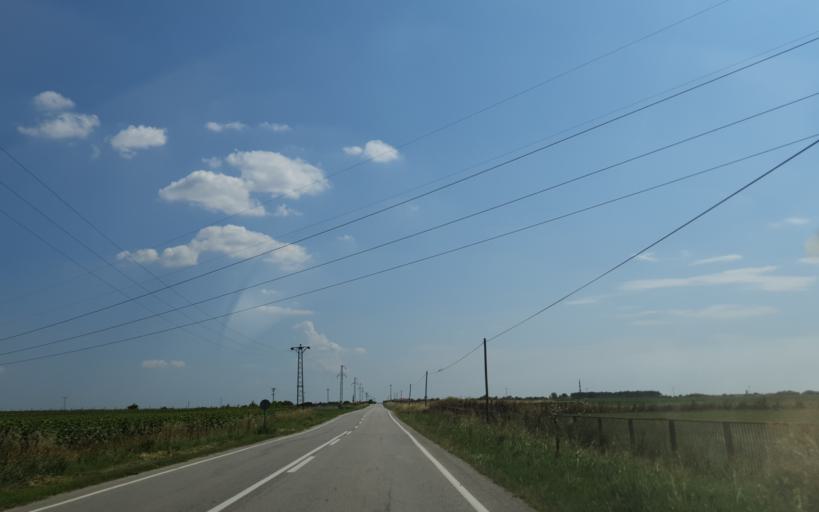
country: TR
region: Kirklareli
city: Buyukkaristiran
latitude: 41.3435
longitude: 27.5469
